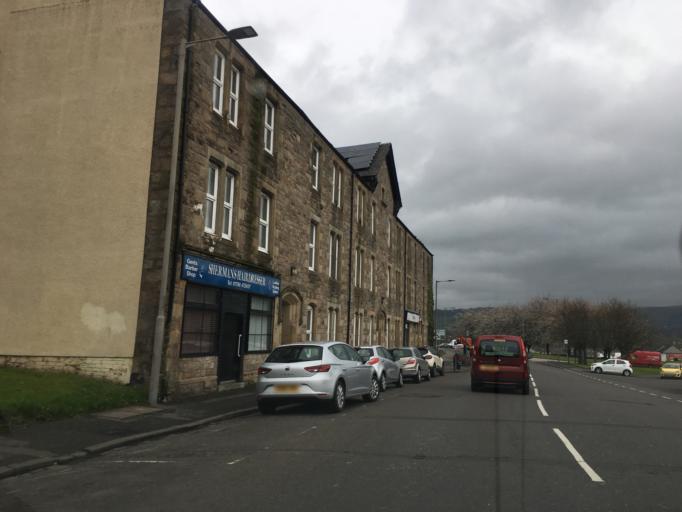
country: GB
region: Scotland
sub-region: Stirling
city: Stirling
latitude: 56.1268
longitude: -3.9413
